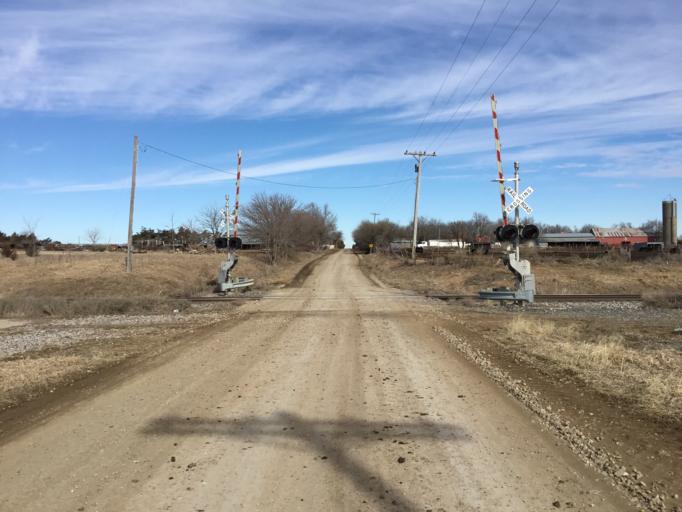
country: US
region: Kansas
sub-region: Geary County
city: Grandview Plaza
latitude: 38.8294
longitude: -96.6680
